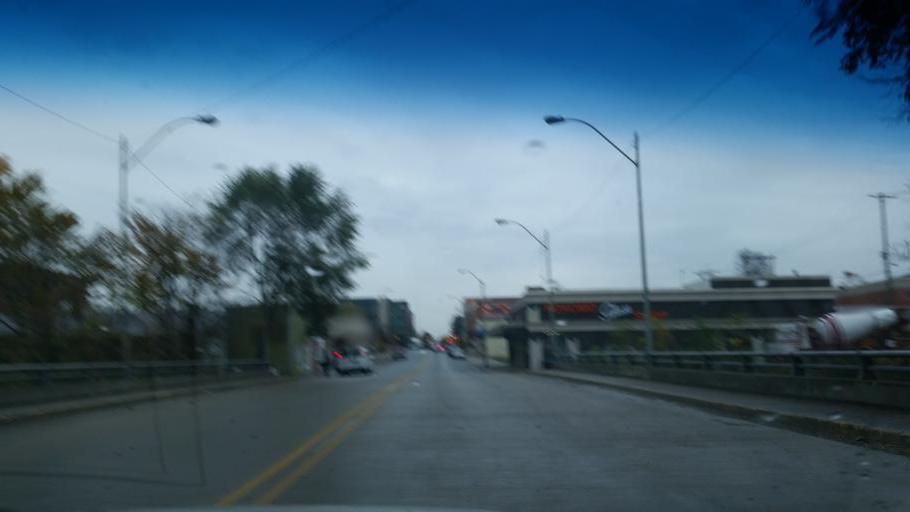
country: US
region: Indiana
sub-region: Howard County
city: Kokomo
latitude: 40.4841
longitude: -86.1300
